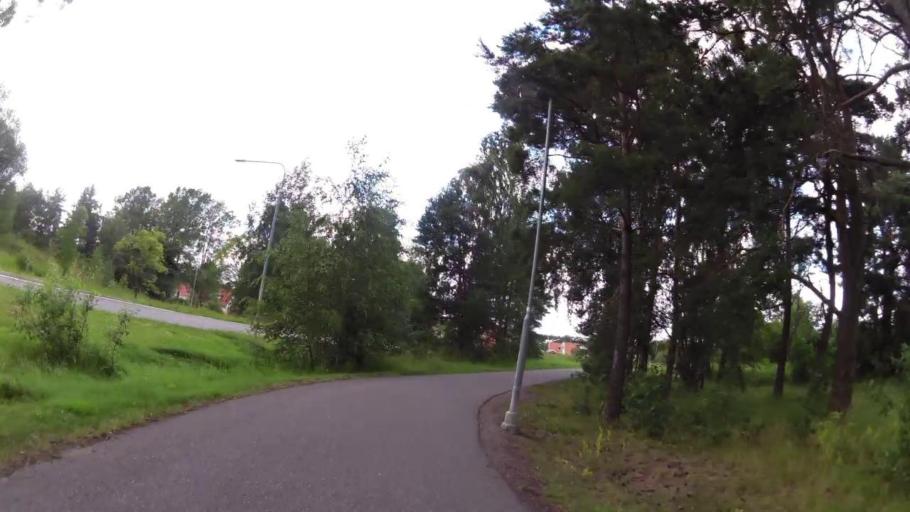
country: SE
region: OEstergoetland
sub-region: Linkopings Kommun
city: Ekangen
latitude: 58.4289
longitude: 15.6767
